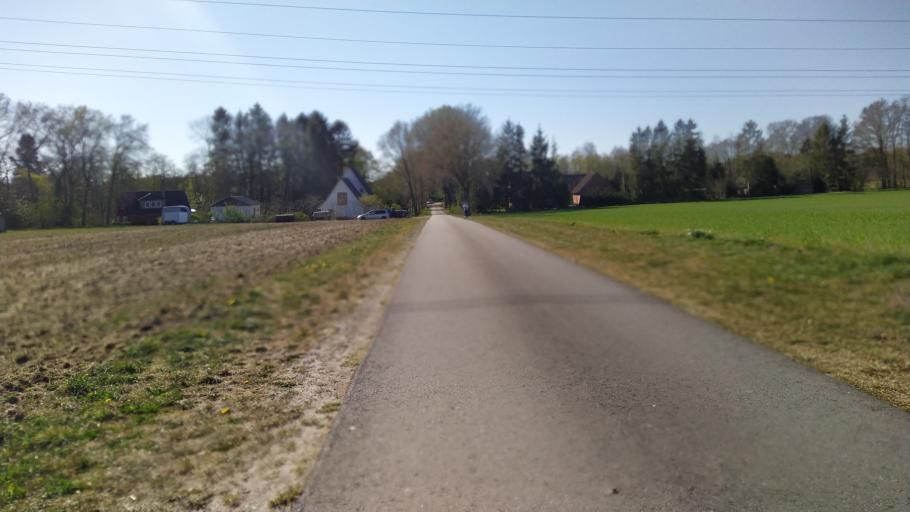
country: DE
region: Lower Saxony
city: Heeslingen
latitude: 53.3318
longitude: 9.3875
